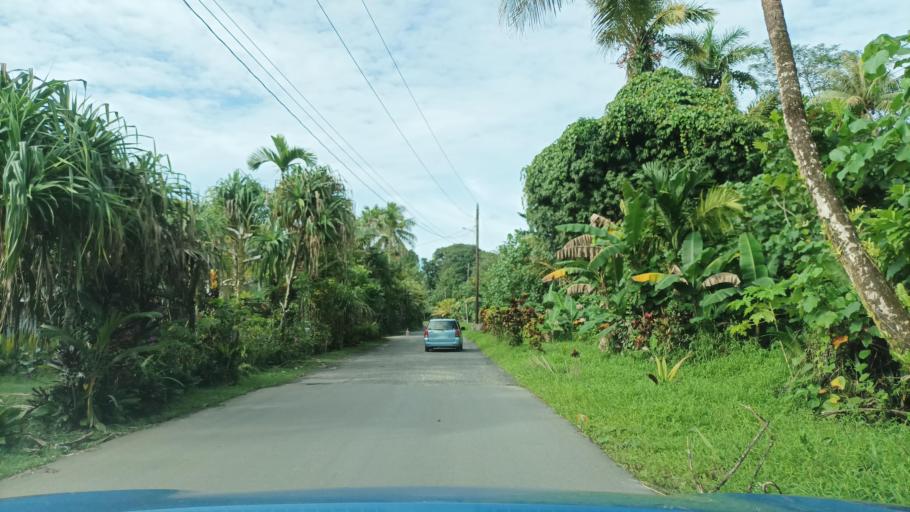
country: FM
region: Pohnpei
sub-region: Kolonia Municipality
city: Kolonia
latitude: 6.9489
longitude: 158.2256
